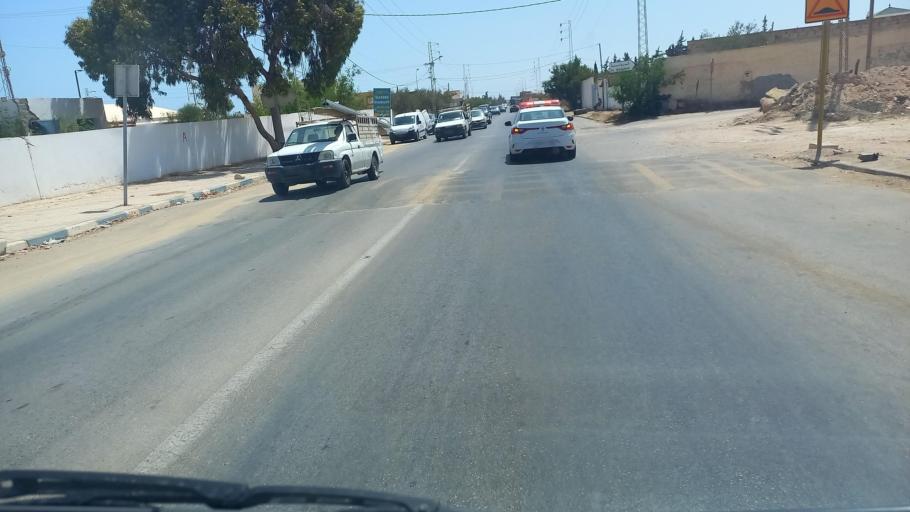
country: TN
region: Madanin
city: Zarzis
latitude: 33.5406
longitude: 11.0778
